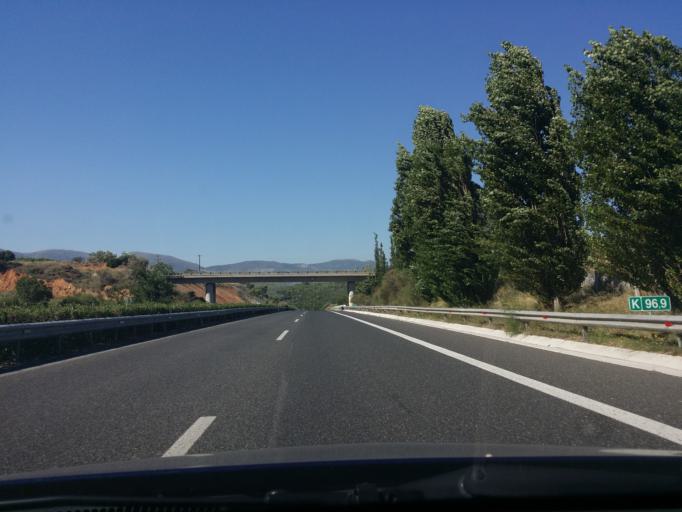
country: GR
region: Peloponnese
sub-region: Nomos Korinthias
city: Khiliomodhi
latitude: 37.8527
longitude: 22.8304
